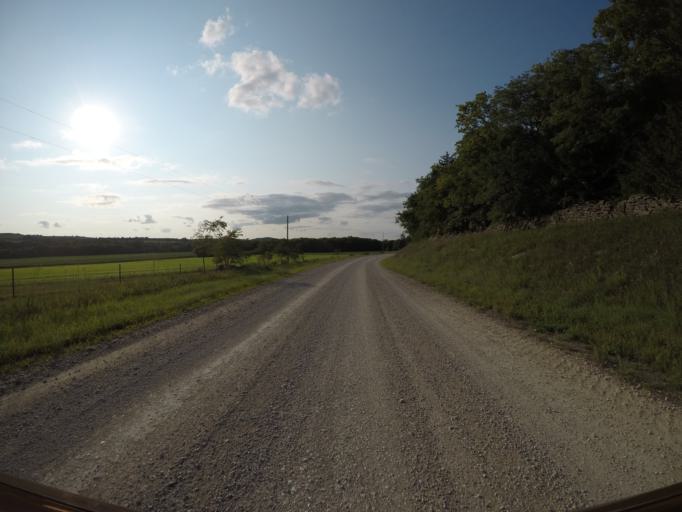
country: US
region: Kansas
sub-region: Wabaunsee County
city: Alma
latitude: 38.9460
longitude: -96.2401
